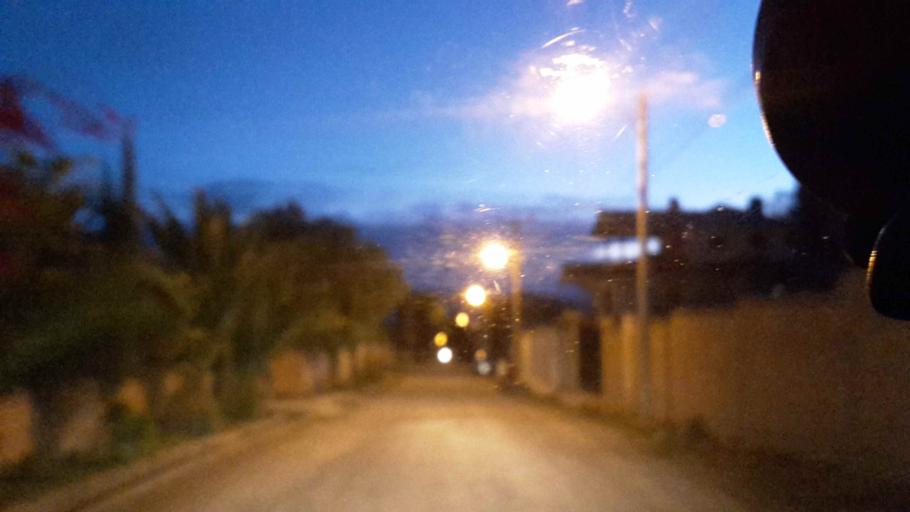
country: BO
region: Cochabamba
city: Cochabamba
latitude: -17.3307
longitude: -66.2175
